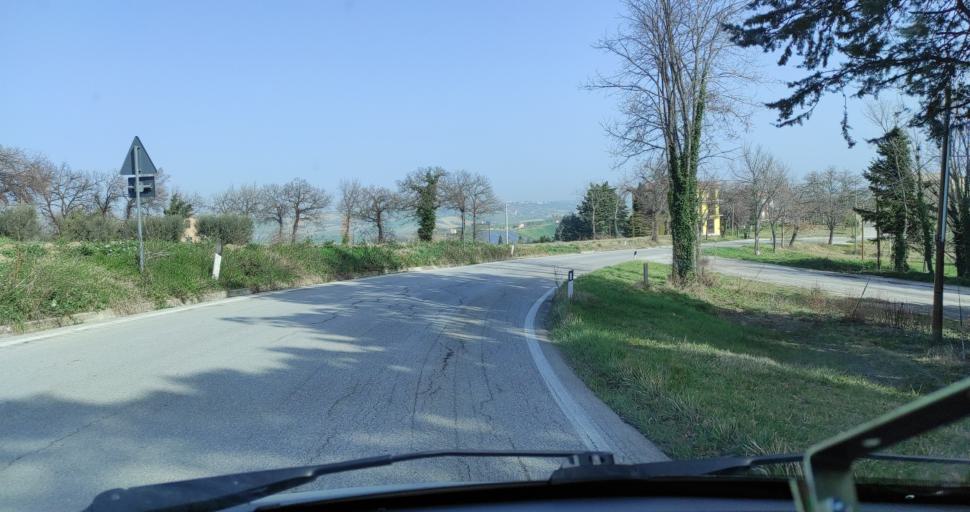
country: IT
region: The Marches
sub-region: Provincia di Macerata
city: Loro Piceno
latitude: 43.1720
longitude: 13.4261
